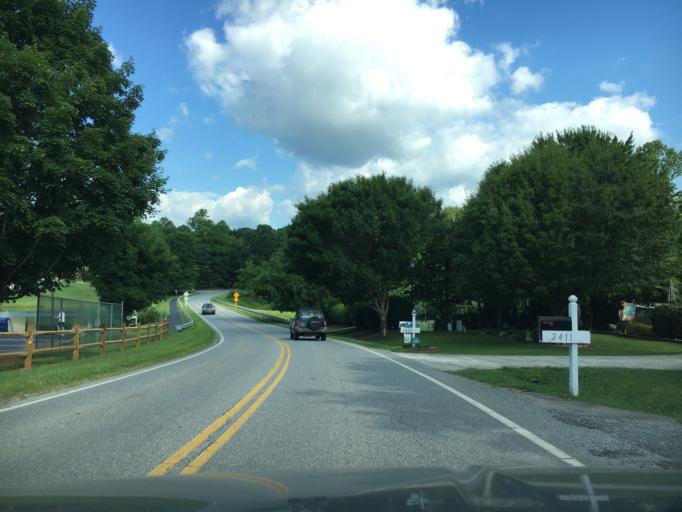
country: US
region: Virginia
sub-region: Bedford County
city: Forest
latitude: 37.3839
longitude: -79.2559
